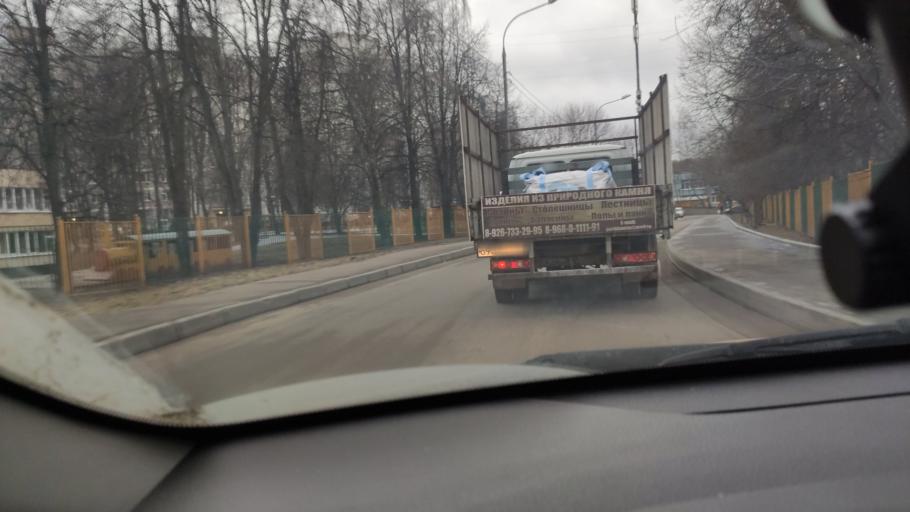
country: RU
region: Moscow
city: Chertanovo Yuzhnoye
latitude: 55.6009
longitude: 37.5844
